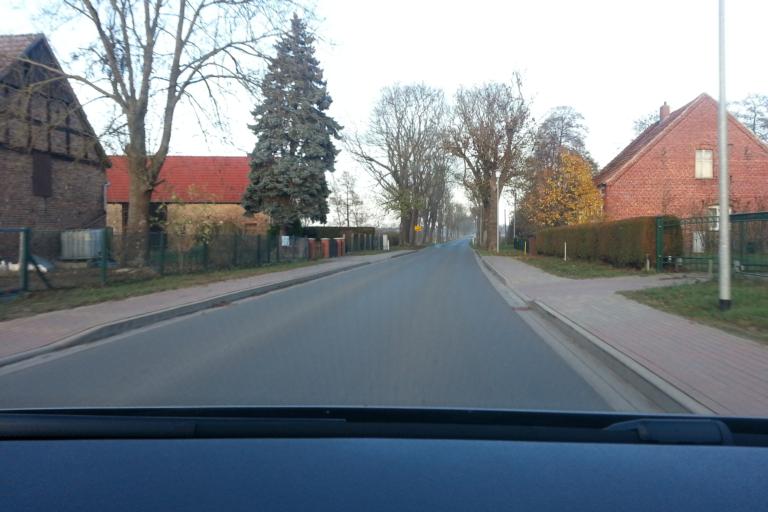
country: DE
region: Mecklenburg-Vorpommern
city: Ferdinandshof
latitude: 53.6447
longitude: 13.8614
